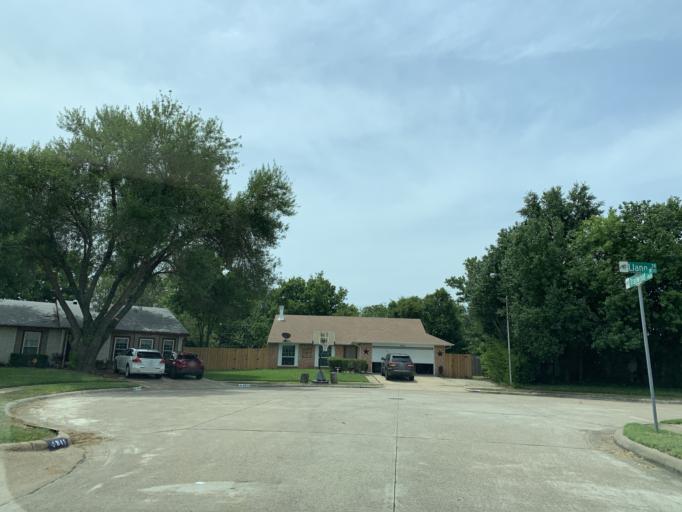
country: US
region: Texas
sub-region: Dallas County
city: Cedar Hill
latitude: 32.6535
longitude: -97.0159
